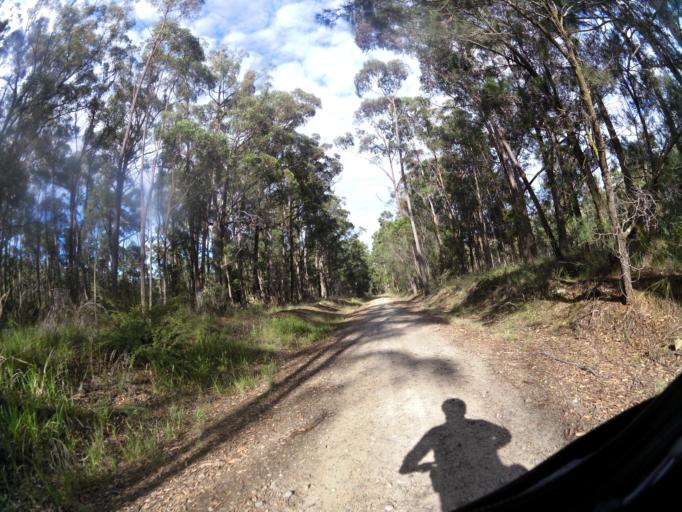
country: AU
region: Victoria
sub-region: East Gippsland
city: Lakes Entrance
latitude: -37.7448
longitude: 148.3778
